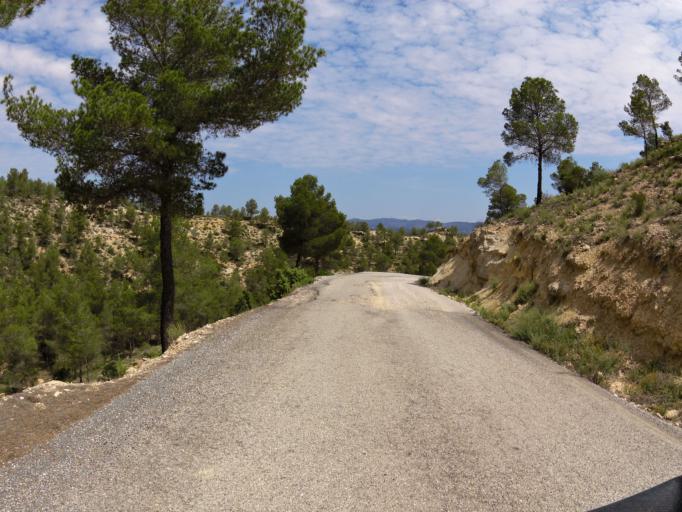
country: ES
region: Castille-La Mancha
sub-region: Provincia de Albacete
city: Casas Ibanez
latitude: 39.3664
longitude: -1.4620
